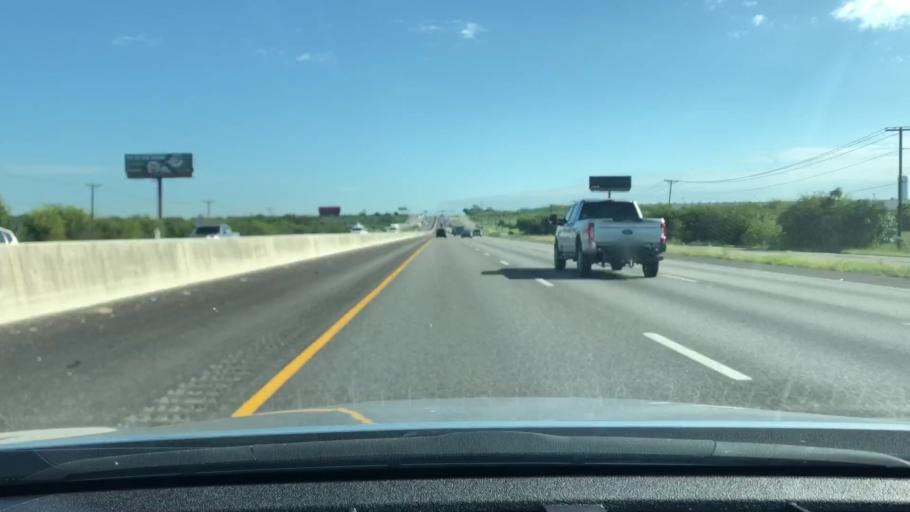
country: US
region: Texas
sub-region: Guadalupe County
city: Lake Dunlap
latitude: 29.7349
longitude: -98.0709
